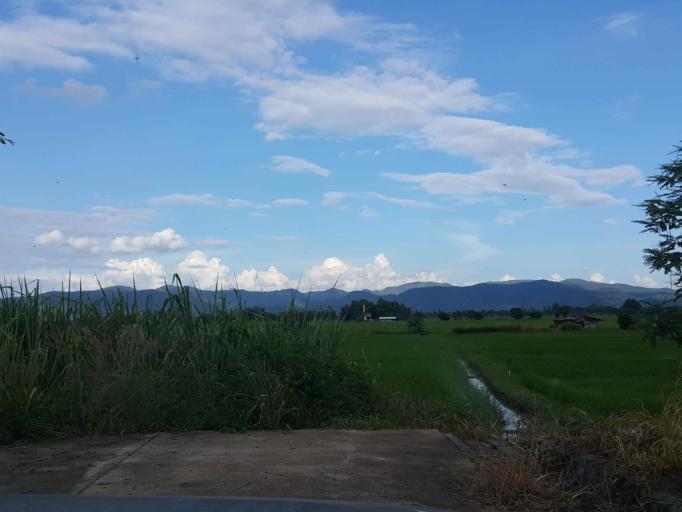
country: TH
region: Chiang Mai
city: Mae Taeng
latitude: 19.0000
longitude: 98.9487
